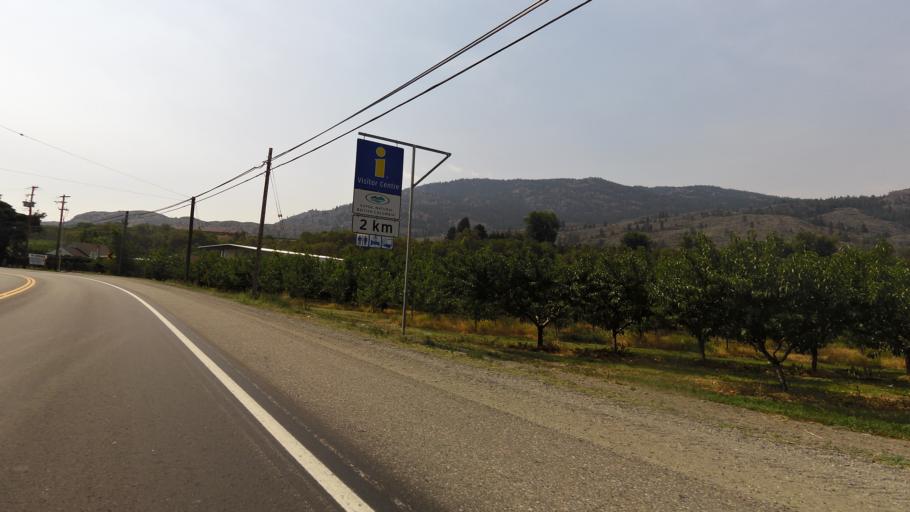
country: CA
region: British Columbia
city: Osoyoos
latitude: 49.0486
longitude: -119.4981
